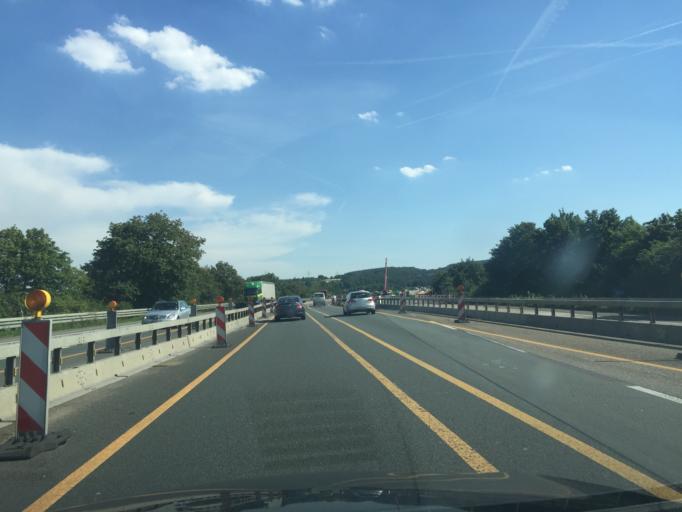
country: DE
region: Hesse
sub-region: Regierungsbezirk Giessen
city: Wetzlar
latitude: 50.5786
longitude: 8.5417
